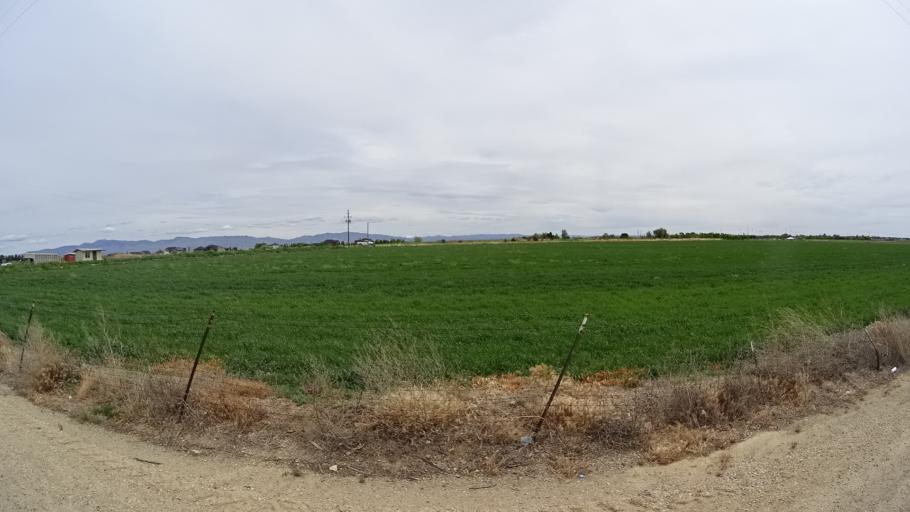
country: US
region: Idaho
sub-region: Ada County
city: Meridian
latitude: 43.5494
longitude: -116.3745
